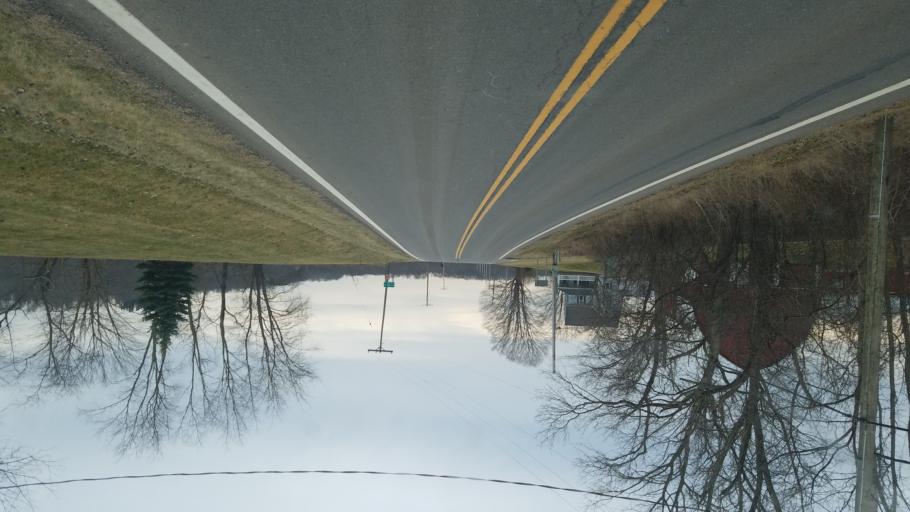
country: US
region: Ohio
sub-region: Richland County
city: Lincoln Heights
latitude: 40.7273
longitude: -82.3699
